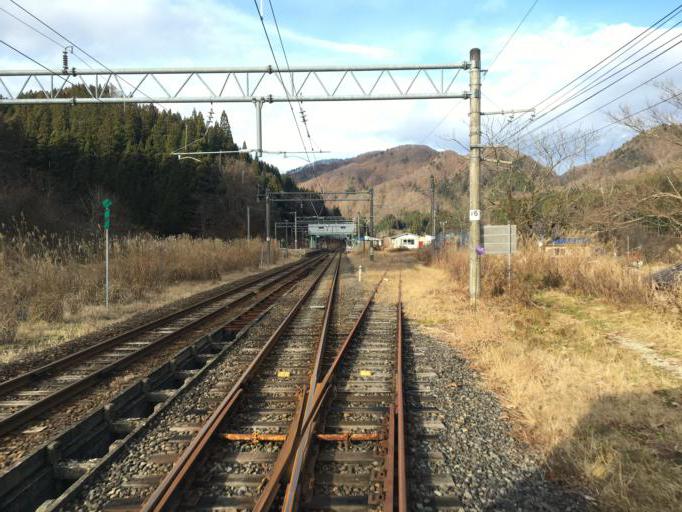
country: JP
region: Akita
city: Yuzawa
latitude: 38.9916
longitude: 140.3613
